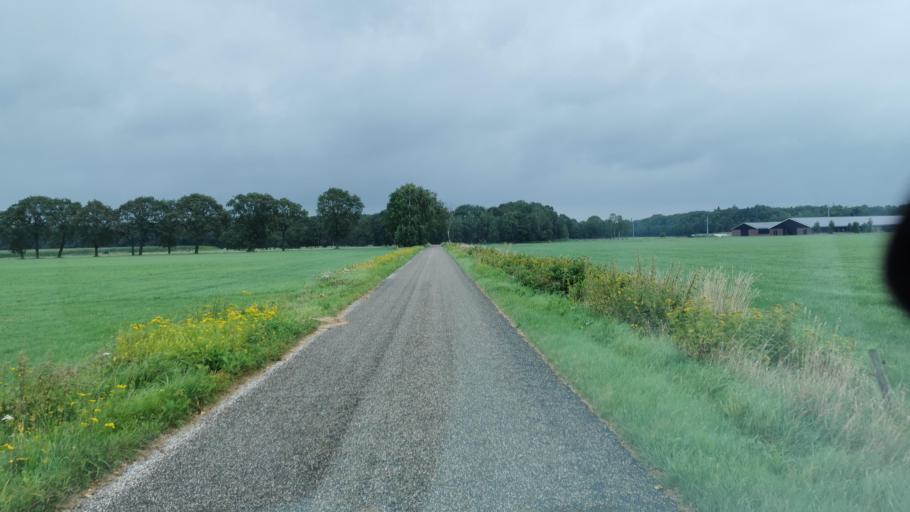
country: NL
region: Overijssel
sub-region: Gemeente Losser
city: Losser
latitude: 52.2360
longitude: 6.9891
